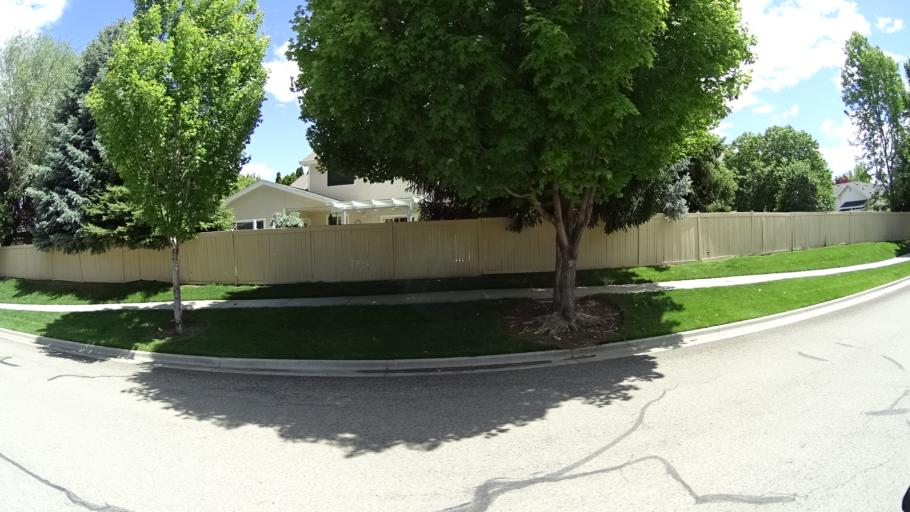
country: US
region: Idaho
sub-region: Ada County
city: Eagle
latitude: 43.6584
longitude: -116.3617
